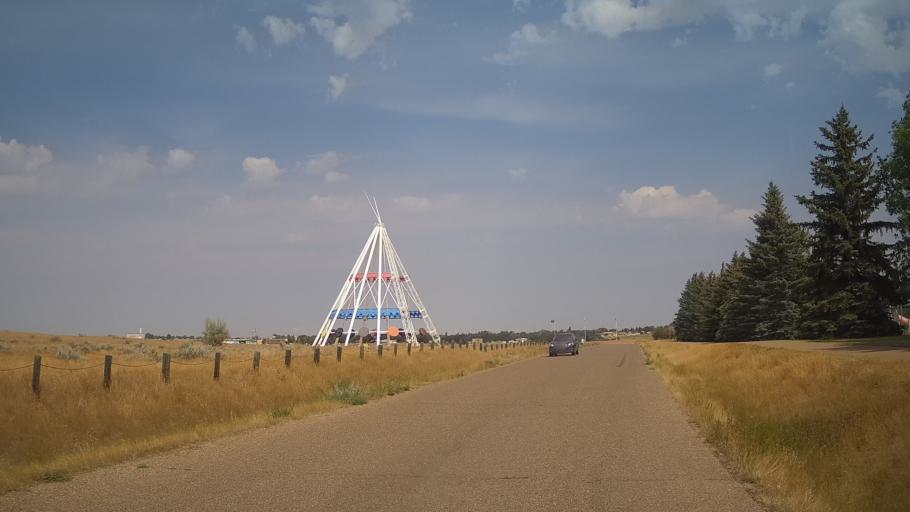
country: CA
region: Alberta
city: Medicine Hat
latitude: 50.0128
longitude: -110.6904
